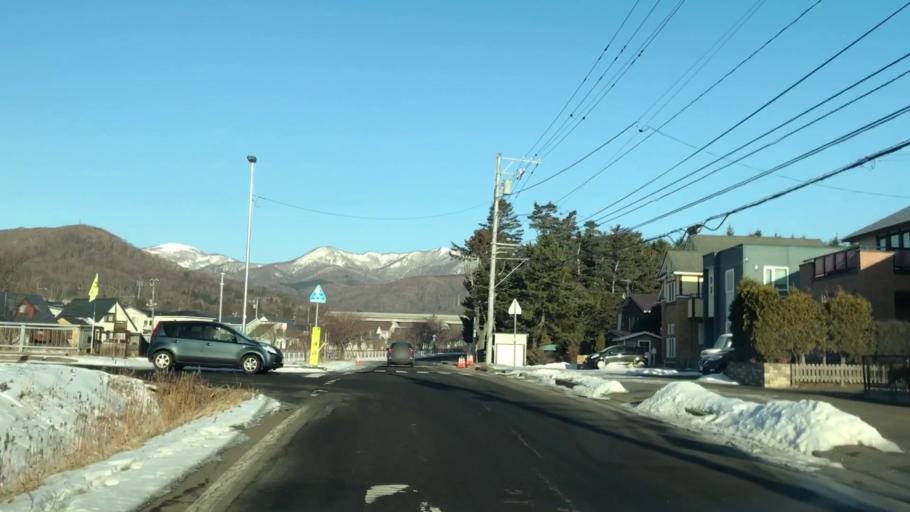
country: JP
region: Hokkaido
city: Muroran
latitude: 42.3865
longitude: 141.0702
